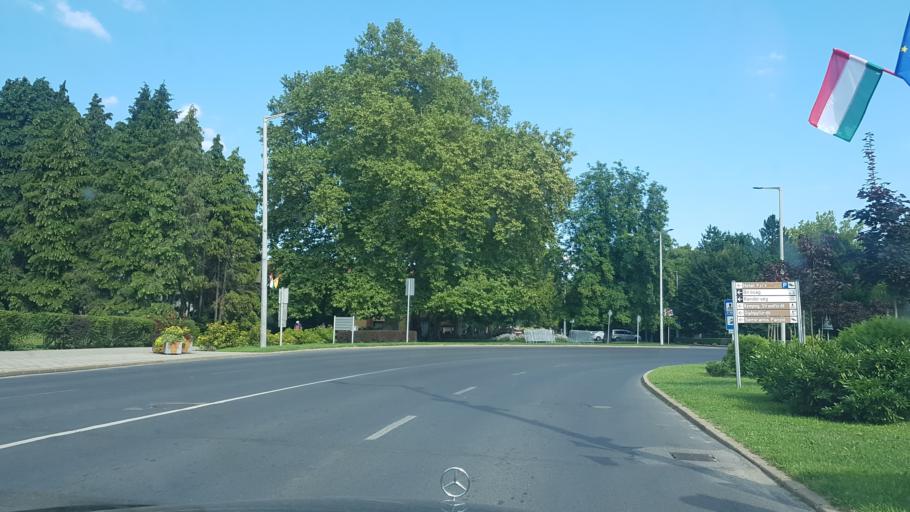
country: HU
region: Somogy
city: Nagyatad
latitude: 46.2296
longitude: 17.3621
